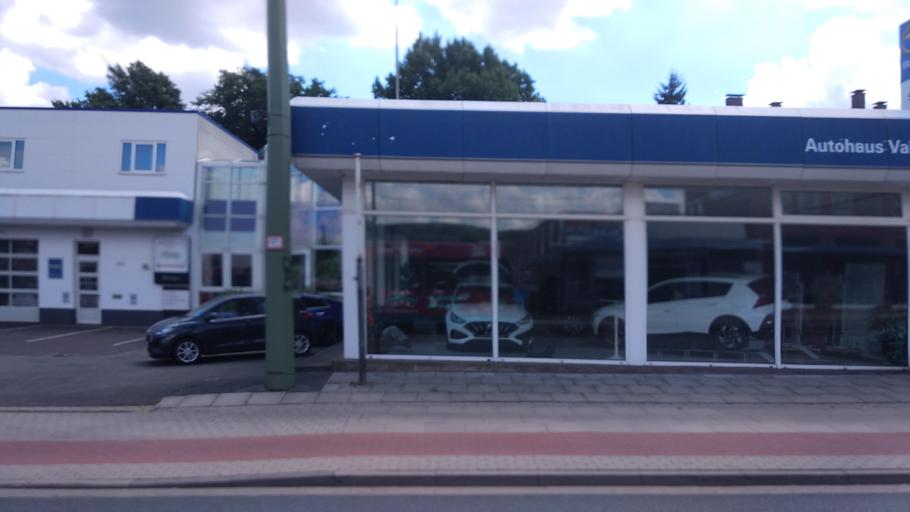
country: DE
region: North Rhine-Westphalia
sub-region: Regierungsbezirk Detmold
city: Bielefeld
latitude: 52.0065
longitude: 8.5121
